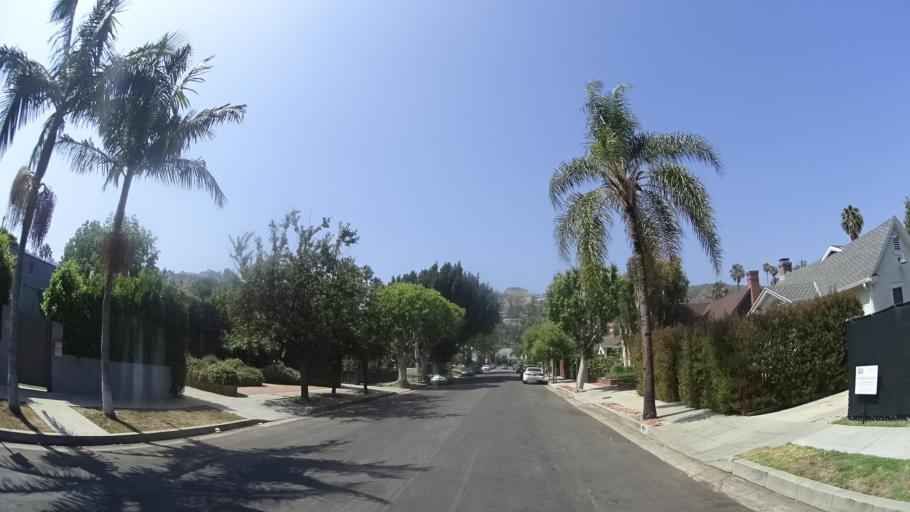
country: US
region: California
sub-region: Los Angeles County
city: West Hollywood
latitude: 34.0999
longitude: -118.3572
